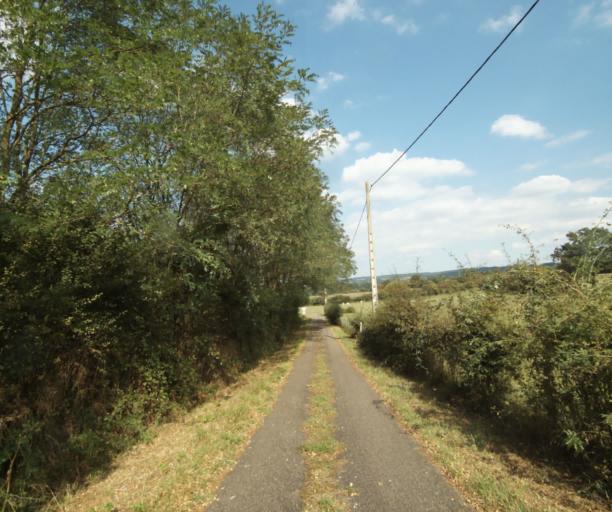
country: FR
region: Bourgogne
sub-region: Departement de Saone-et-Loire
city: Palinges
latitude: 46.4858
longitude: 4.2259
